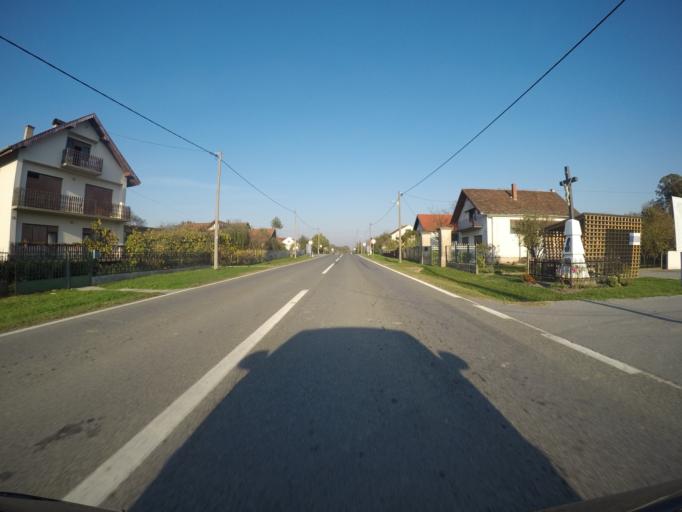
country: HR
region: Virovitick-Podravska
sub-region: Grad Virovitica
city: Virovitica
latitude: 45.8890
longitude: 17.4185
